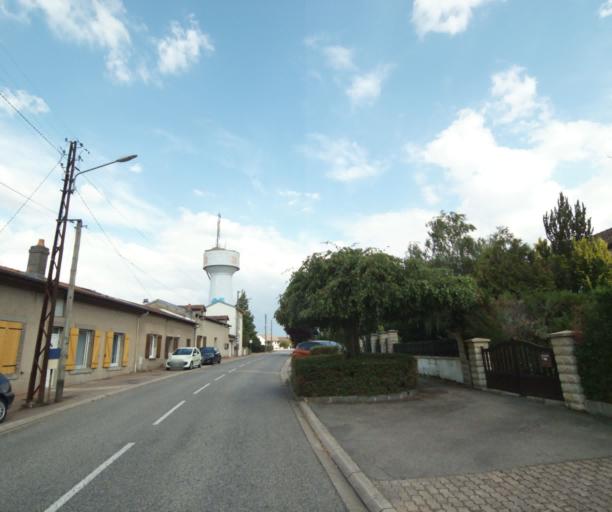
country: FR
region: Lorraine
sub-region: Departement de Meurthe-et-Moselle
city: Chanteheux
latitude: 48.5731
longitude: 6.5333
